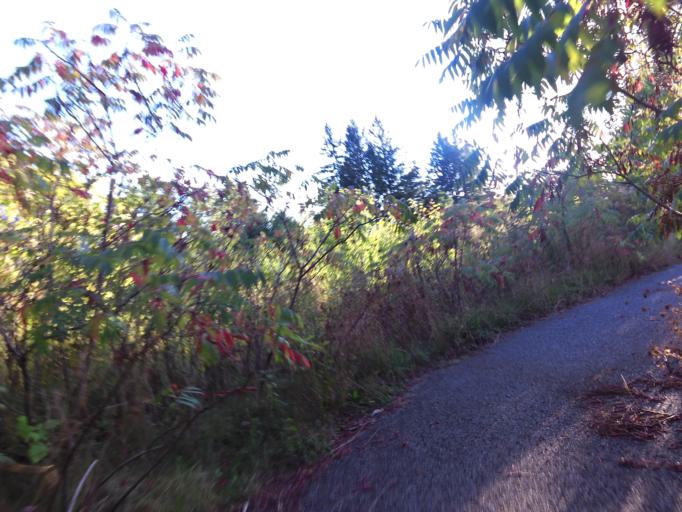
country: CA
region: Ontario
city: Ottawa
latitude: 45.4096
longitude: -75.7728
